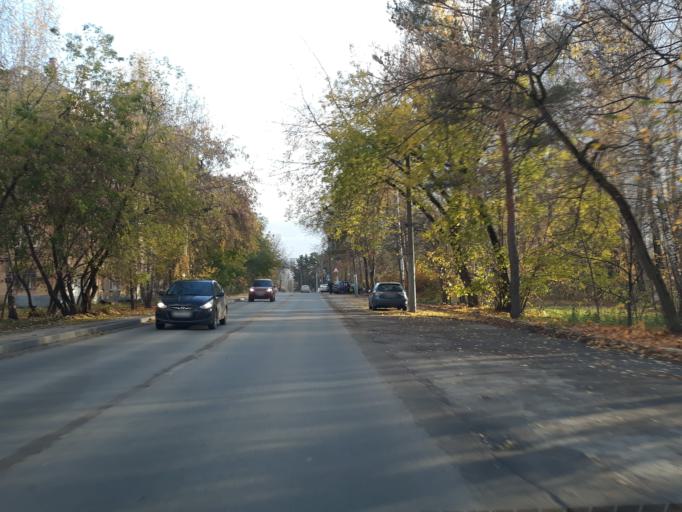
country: RU
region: Nizjnij Novgorod
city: Neklyudovo
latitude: 56.3411
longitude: 43.8661
